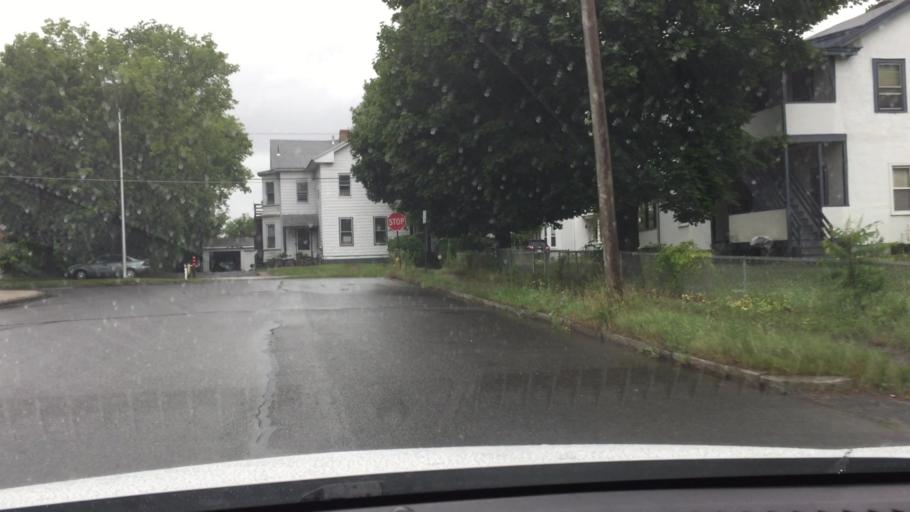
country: US
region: Massachusetts
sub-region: Berkshire County
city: Pittsfield
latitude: 42.4530
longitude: -73.2563
